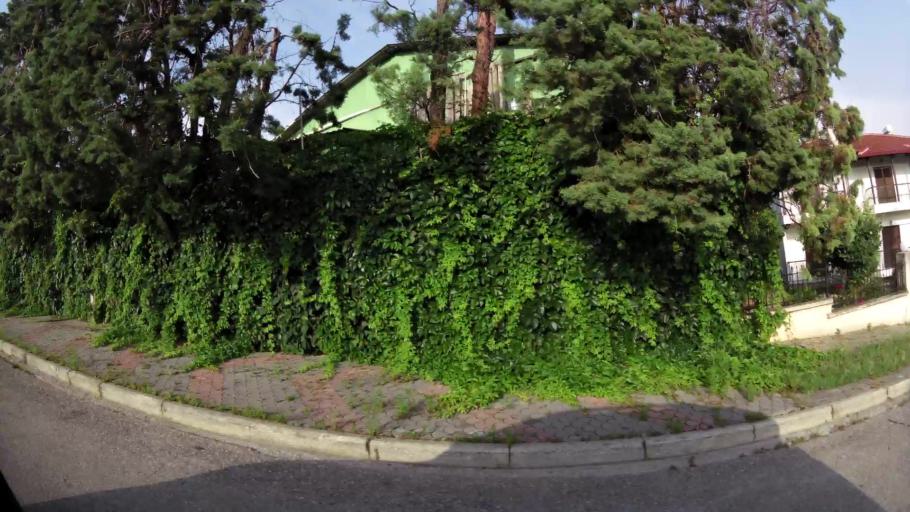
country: GR
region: Central Macedonia
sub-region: Nomos Thessalonikis
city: Oraiokastro
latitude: 40.7249
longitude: 22.9042
